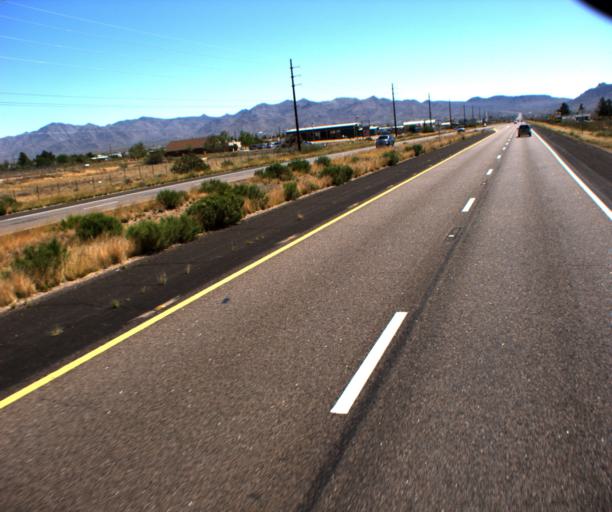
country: US
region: Arizona
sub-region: Mohave County
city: Golden Valley
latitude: 35.2222
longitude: -114.2218
